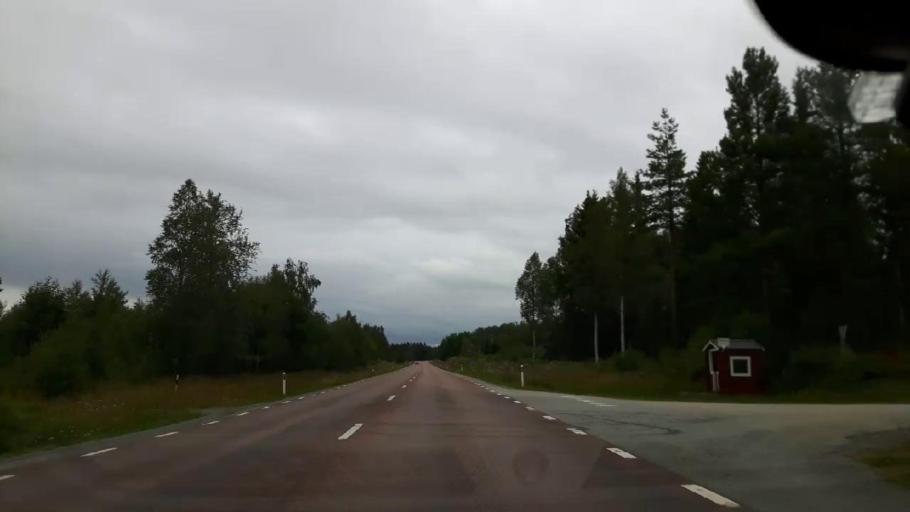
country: SE
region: Jaemtland
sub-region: Bergs Kommun
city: Hoverberg
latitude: 62.8956
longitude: 14.5240
